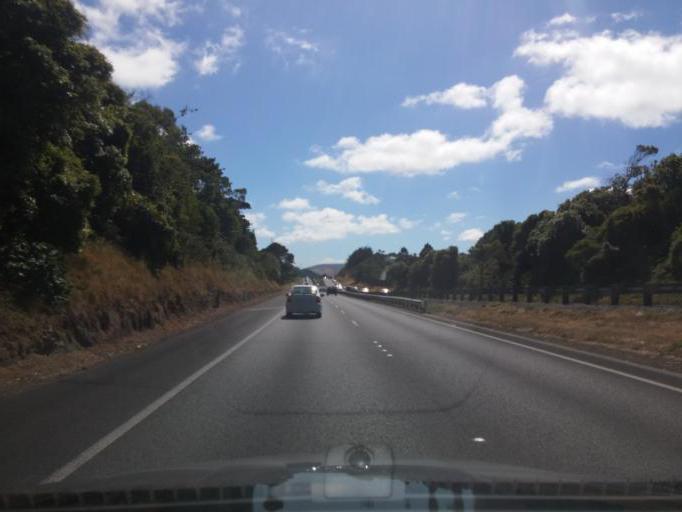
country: NZ
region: Wellington
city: Petone
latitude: -41.2118
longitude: 174.8148
